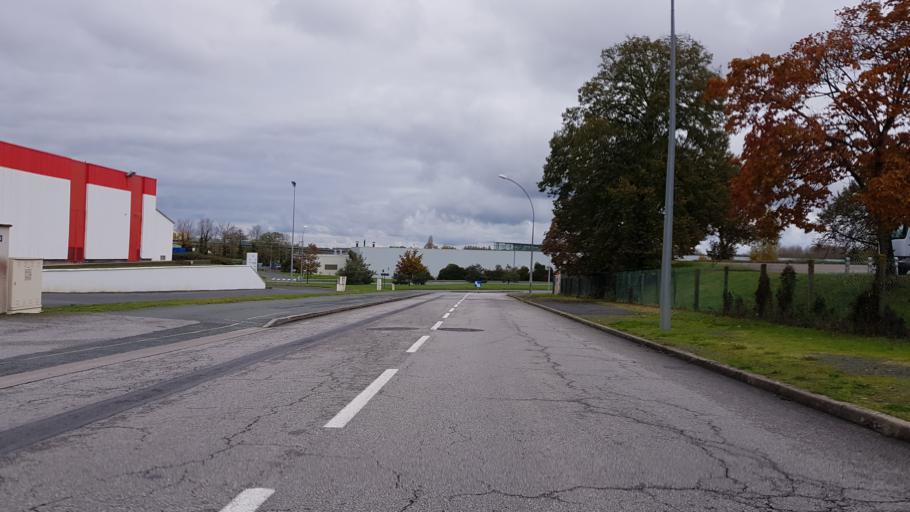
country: FR
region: Poitou-Charentes
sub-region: Departement de la Vienne
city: Chasseneuil-du-Poitou
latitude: 46.6665
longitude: 0.3746
